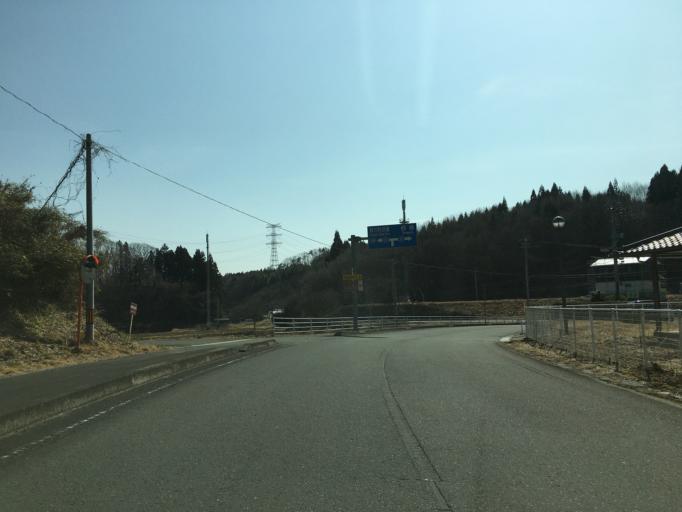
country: JP
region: Fukushima
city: Ishikawa
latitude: 37.0386
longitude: 140.4730
